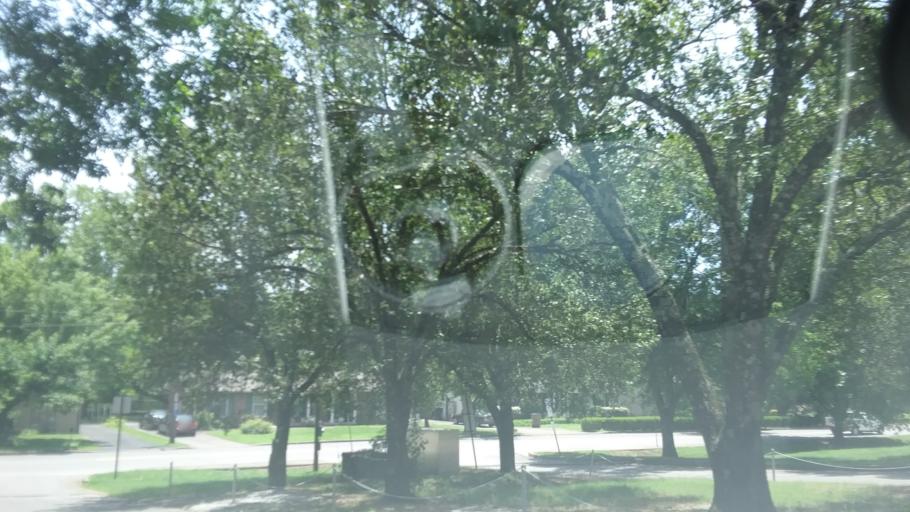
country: US
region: Tennessee
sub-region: Rutherford County
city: La Vergne
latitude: 36.0787
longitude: -86.6302
